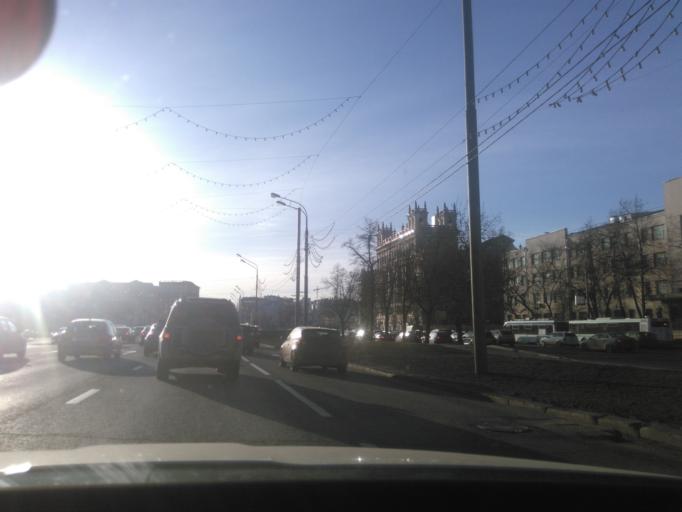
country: RU
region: Moskovskaya
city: Dorogomilovo
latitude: 55.7794
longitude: 37.5787
